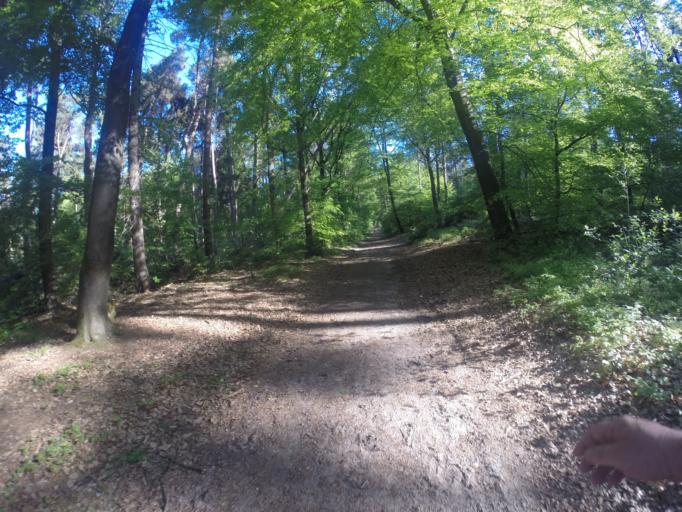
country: NL
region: Gelderland
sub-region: Gemeente Montferland
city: s-Heerenberg
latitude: 51.8870
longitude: 6.2468
